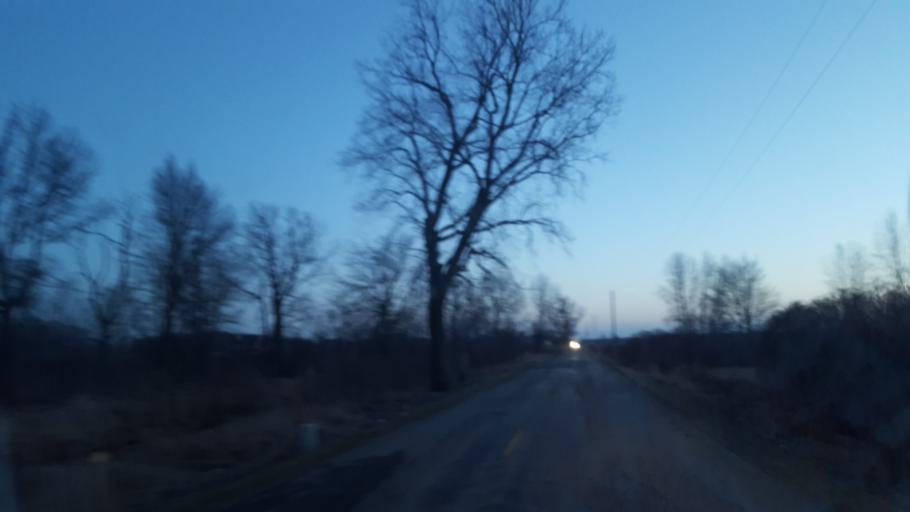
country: US
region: Indiana
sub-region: Kosciusko County
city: Mentone
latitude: 41.2795
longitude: -85.9989
